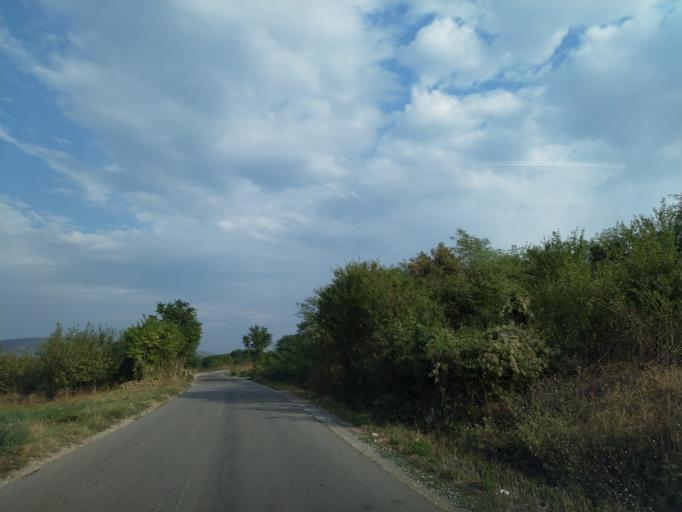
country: RS
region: Central Serbia
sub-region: Pomoravski Okrug
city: Paracin
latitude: 43.8430
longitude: 21.4881
